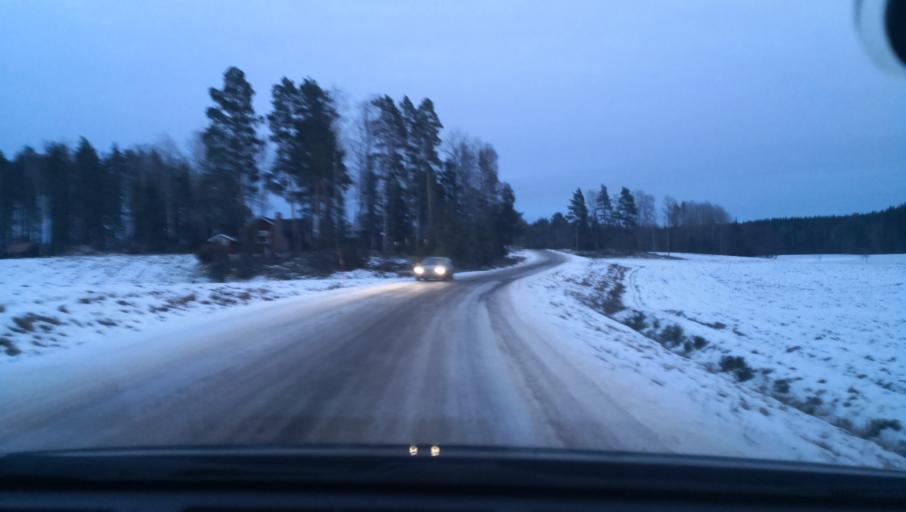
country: SE
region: Dalarna
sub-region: Avesta Kommun
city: Horndal
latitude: 60.2045
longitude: 16.5223
